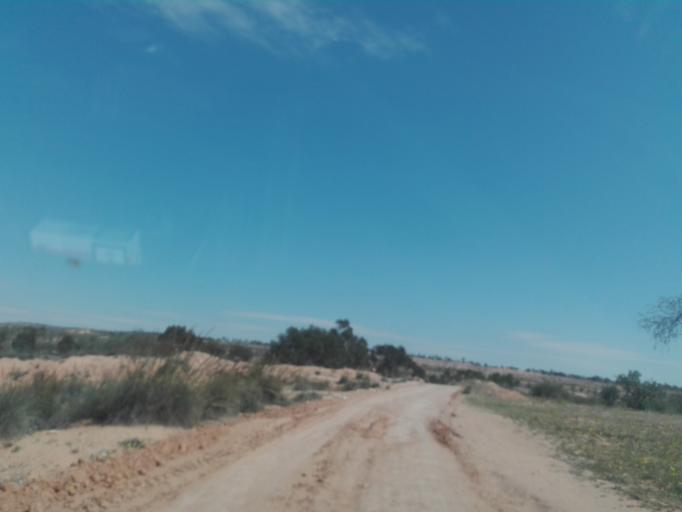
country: TN
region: Safaqis
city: Sfax
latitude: 34.6930
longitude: 10.5300
